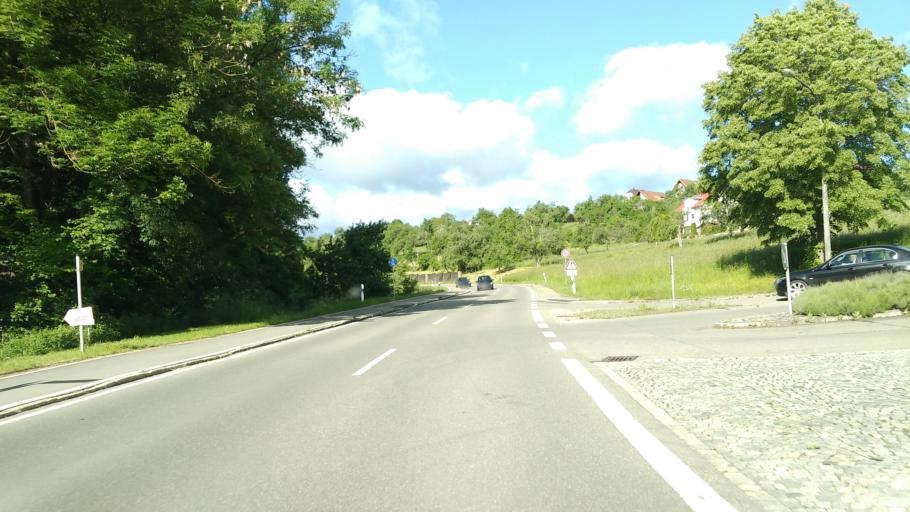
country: DE
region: Baden-Wuerttemberg
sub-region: Tuebingen Region
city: Kusterdingen
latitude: 48.5264
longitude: 9.1270
